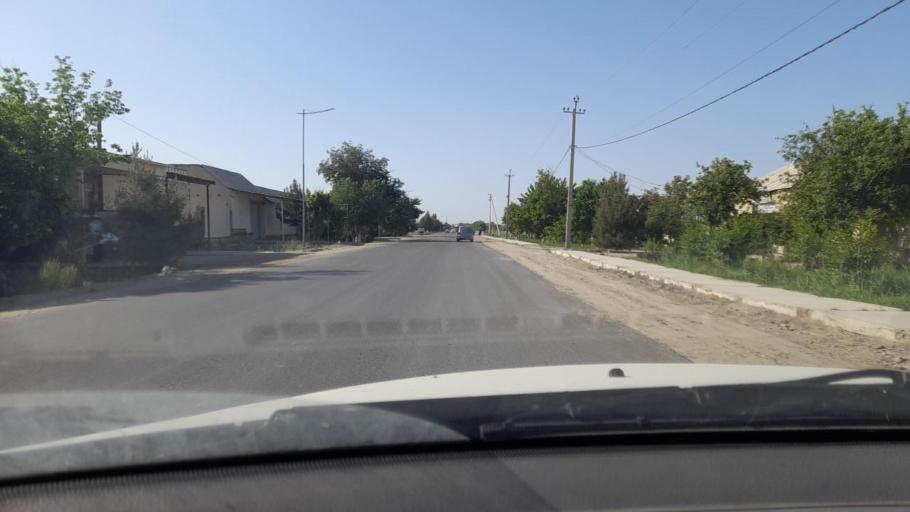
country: UZ
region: Bukhara
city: Romiton
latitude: 40.0736
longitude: 64.3264
